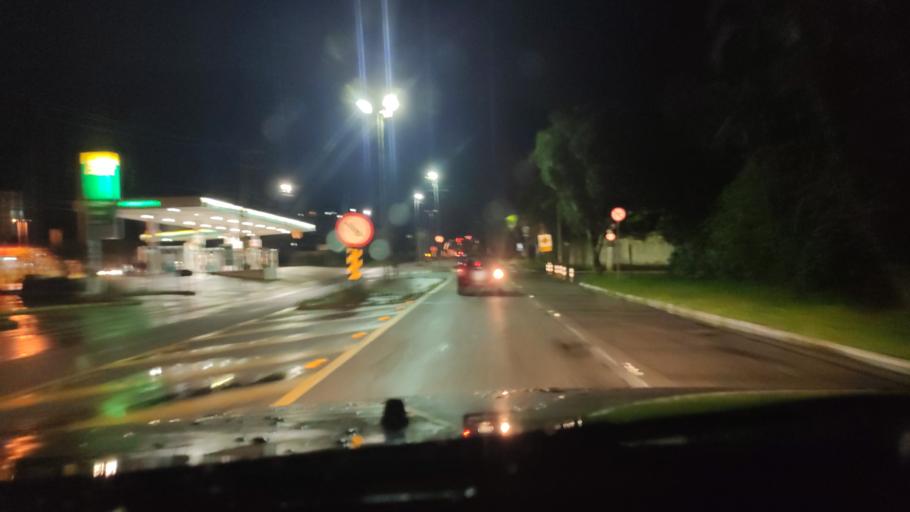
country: BR
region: Sao Paulo
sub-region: Sao Sebastiao
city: Sao Sebastiao
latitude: -23.7321
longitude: -45.4017
